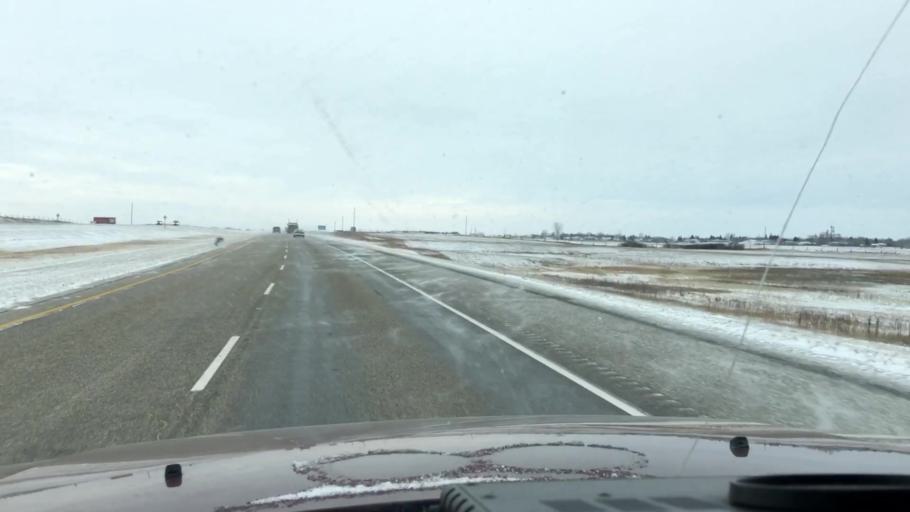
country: CA
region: Saskatchewan
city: Saskatoon
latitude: 51.6447
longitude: -106.4373
